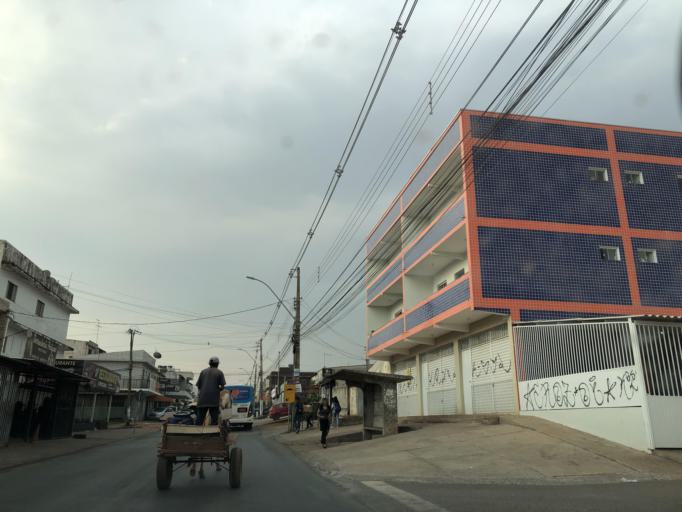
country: BR
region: Federal District
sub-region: Brasilia
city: Brasilia
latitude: -15.9197
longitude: -48.0613
